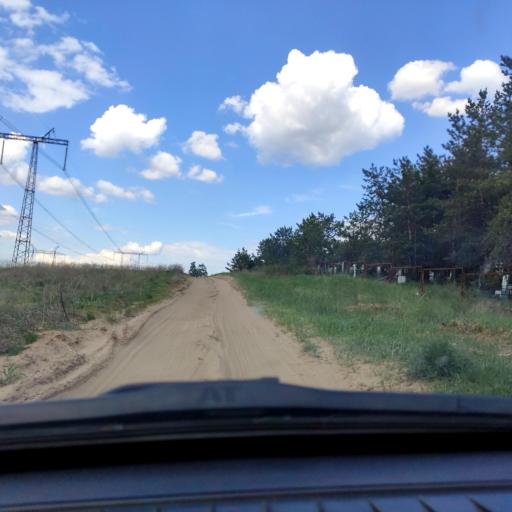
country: RU
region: Samara
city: Zhigulevsk
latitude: 53.5326
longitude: 49.5454
